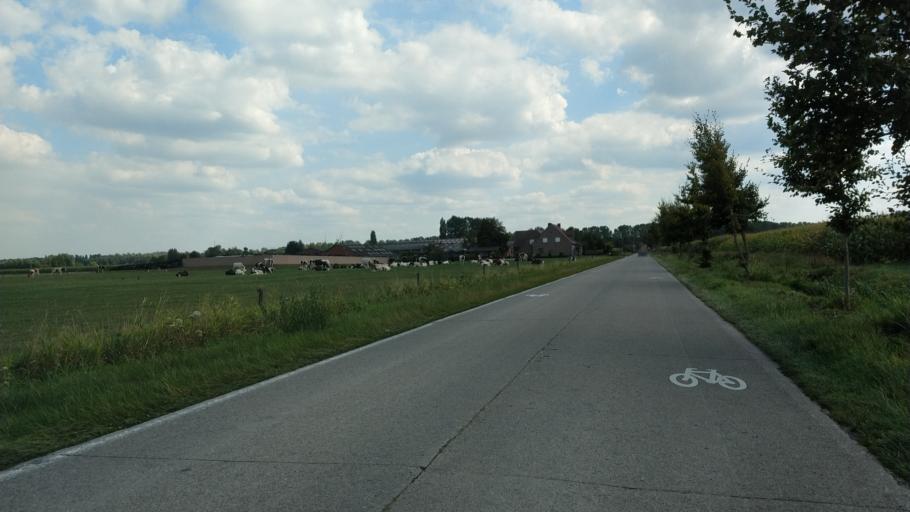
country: BE
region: Flanders
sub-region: Provincie Oost-Vlaanderen
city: Evergem
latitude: 51.1623
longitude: 3.6903
